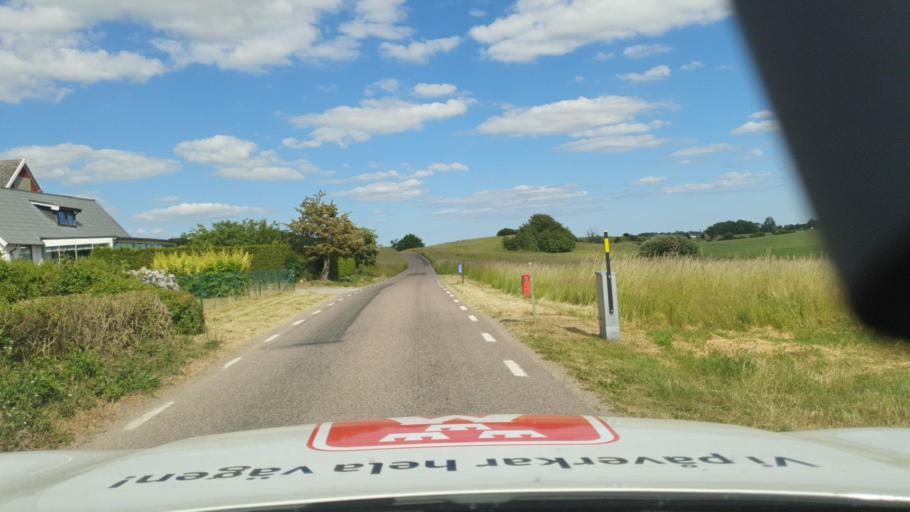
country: SE
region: Skane
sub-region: Ystads Kommun
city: Kopingebro
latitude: 55.4697
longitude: 13.9634
